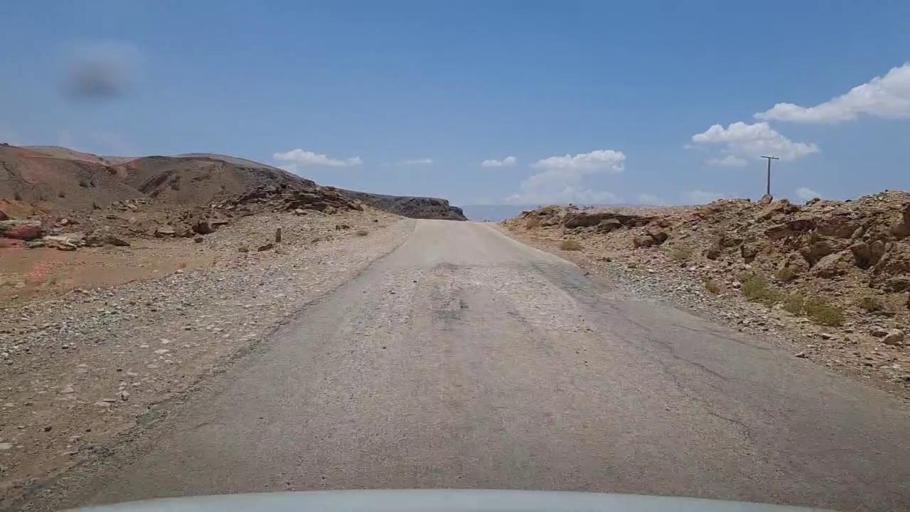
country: PK
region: Sindh
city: Bhan
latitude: 26.3143
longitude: 67.5425
